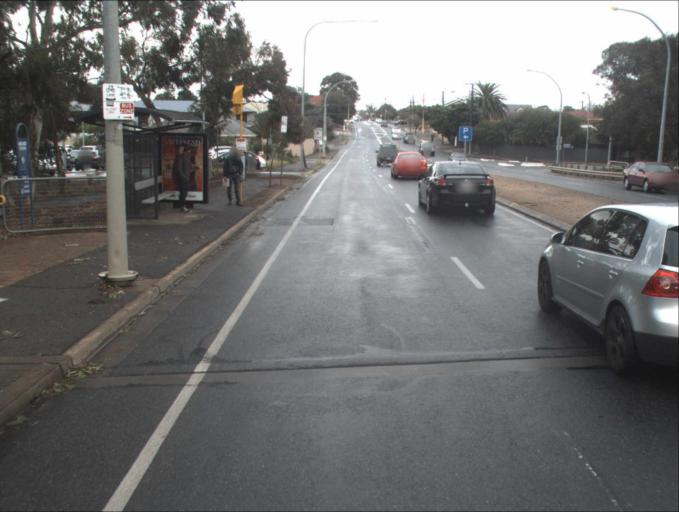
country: AU
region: South Australia
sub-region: Port Adelaide Enfield
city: Klemzig
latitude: -34.8866
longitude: 138.6388
